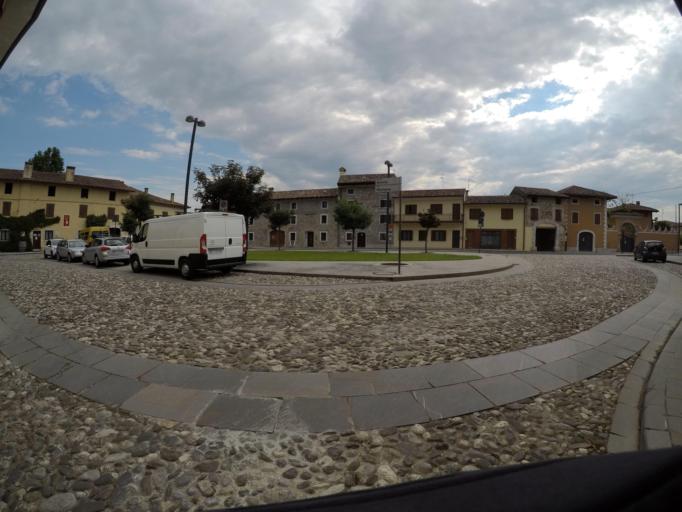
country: IT
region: Friuli Venezia Giulia
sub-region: Provincia di Udine
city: Trivignano Udinese
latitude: 45.9306
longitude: 13.3318
